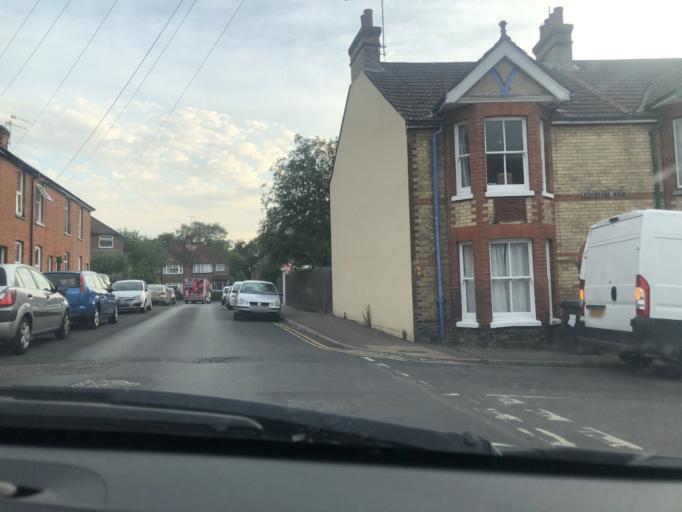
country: GB
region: England
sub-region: Kent
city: Canterbury
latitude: 51.2705
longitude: 1.0751
